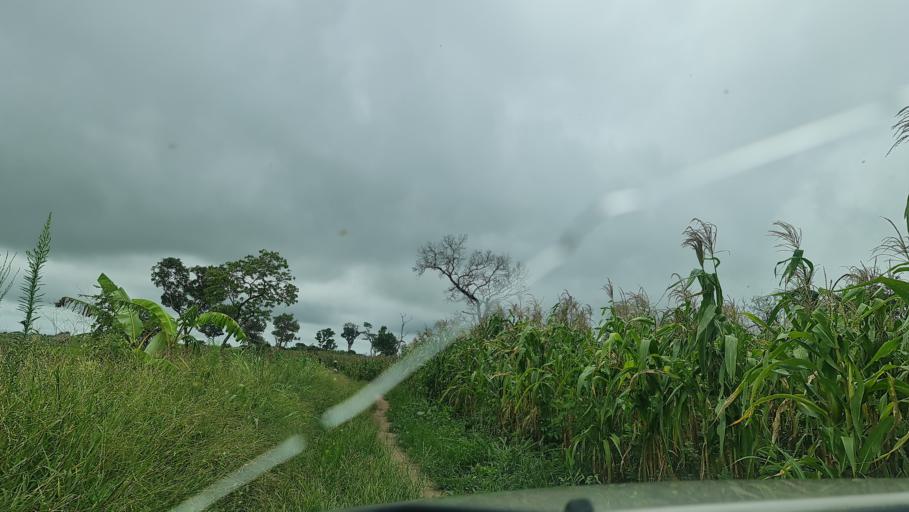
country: MW
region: Southern Region
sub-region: Nsanje District
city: Nsanje
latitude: -17.3403
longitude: 35.7295
